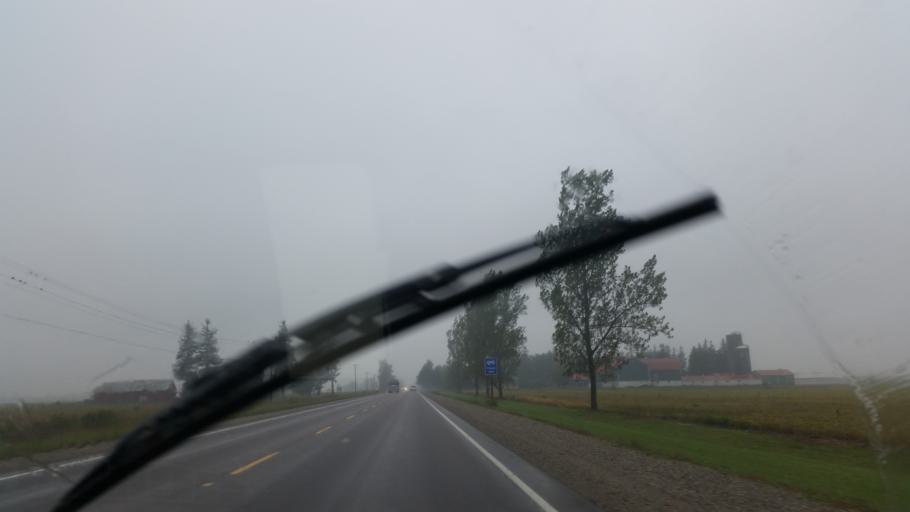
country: CA
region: Ontario
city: Stratford
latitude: 43.3364
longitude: -81.0125
